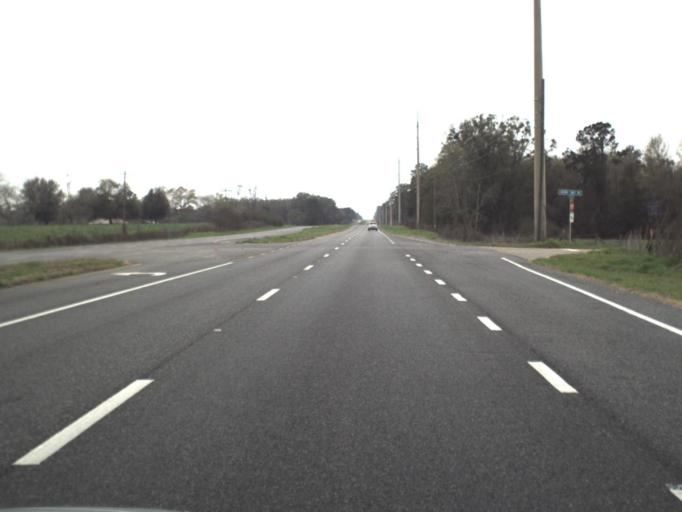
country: US
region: Florida
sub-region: Jefferson County
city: Monticello
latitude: 30.4082
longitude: -83.9818
